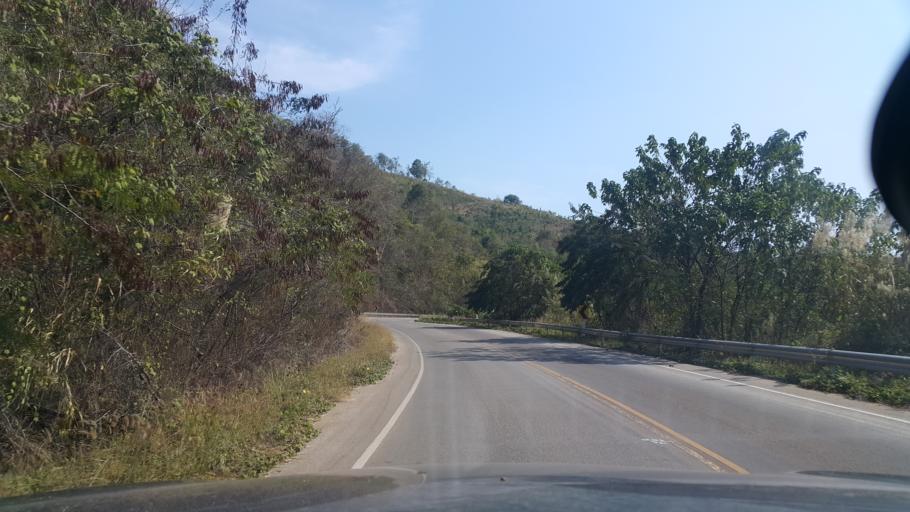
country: TH
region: Loei
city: Pak Chom
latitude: 18.1071
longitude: 102.0060
